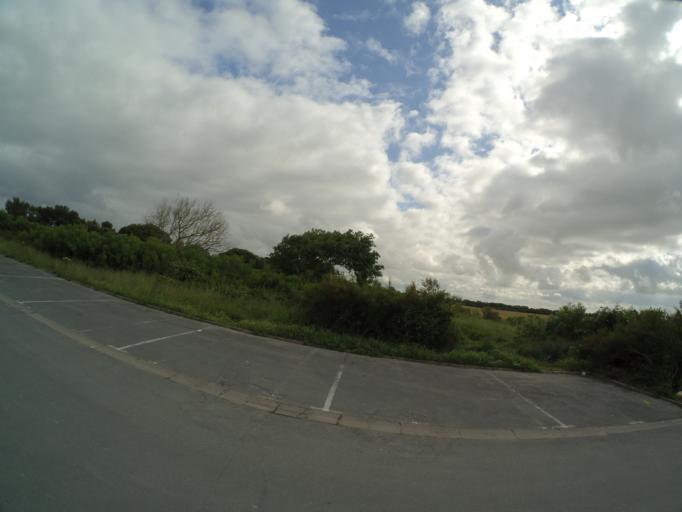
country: FR
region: Poitou-Charentes
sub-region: Departement de la Charente-Maritime
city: Angoulins
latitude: 46.1129
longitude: -1.1230
